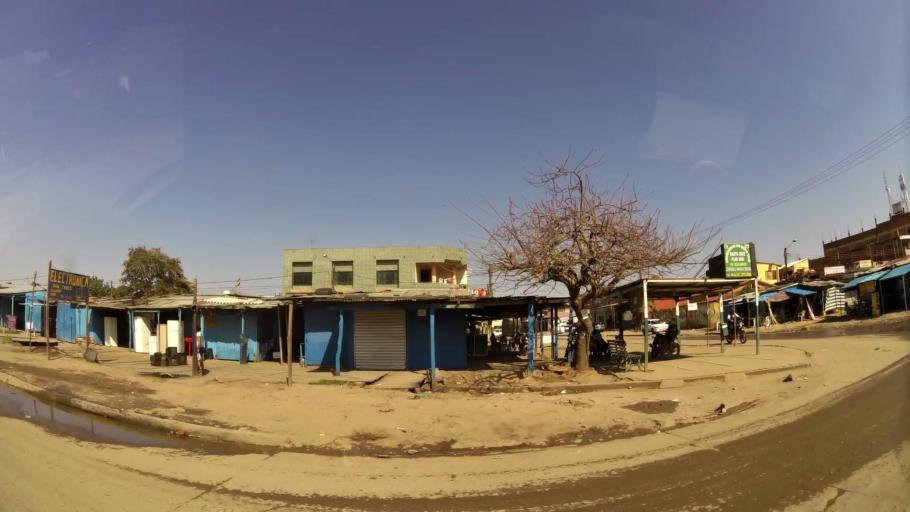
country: BO
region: Santa Cruz
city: Cotoca
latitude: -17.8170
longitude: -63.1160
